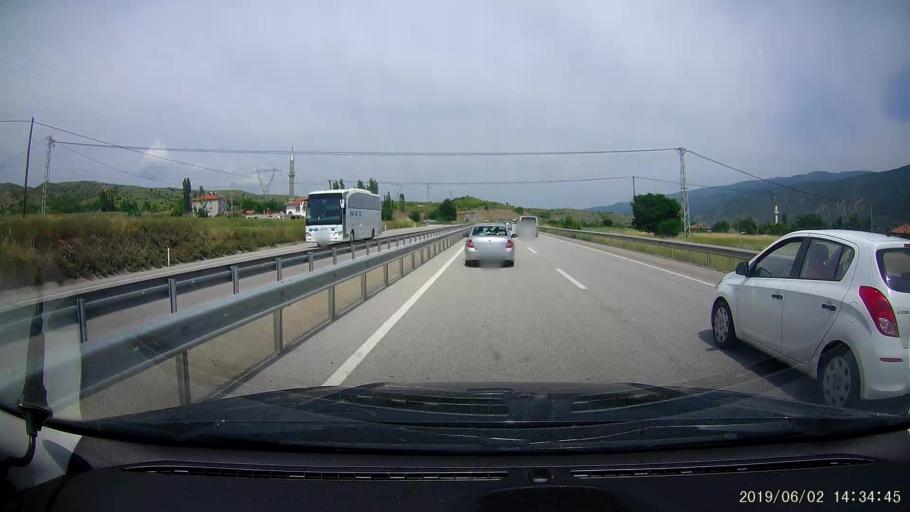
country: TR
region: Kastamonu
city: Tosya
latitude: 41.0400
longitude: 34.1996
